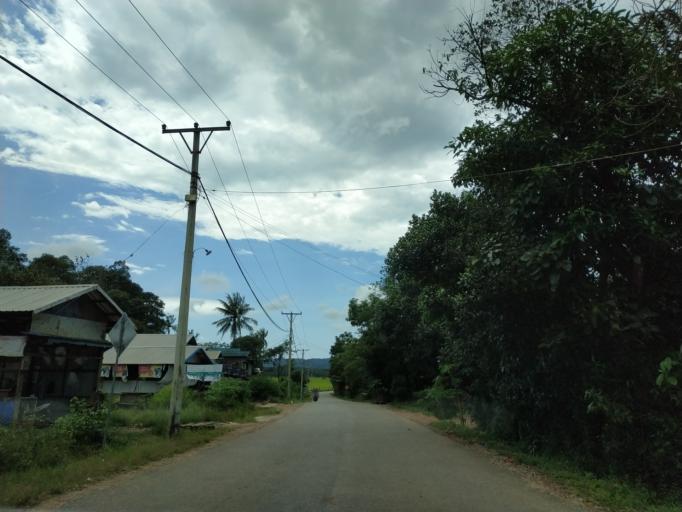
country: MM
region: Tanintharyi
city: Dawei
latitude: 14.1542
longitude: 98.1742
